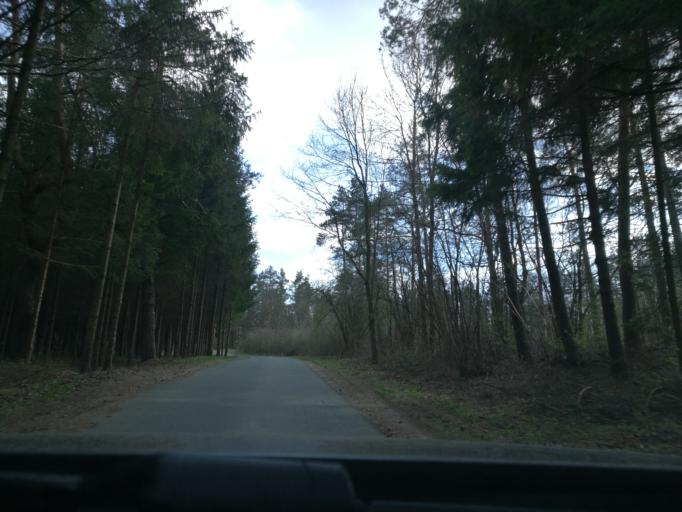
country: DE
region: Bavaria
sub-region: Upper Franconia
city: Heiligenstadt
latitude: 49.8381
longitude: 11.1352
